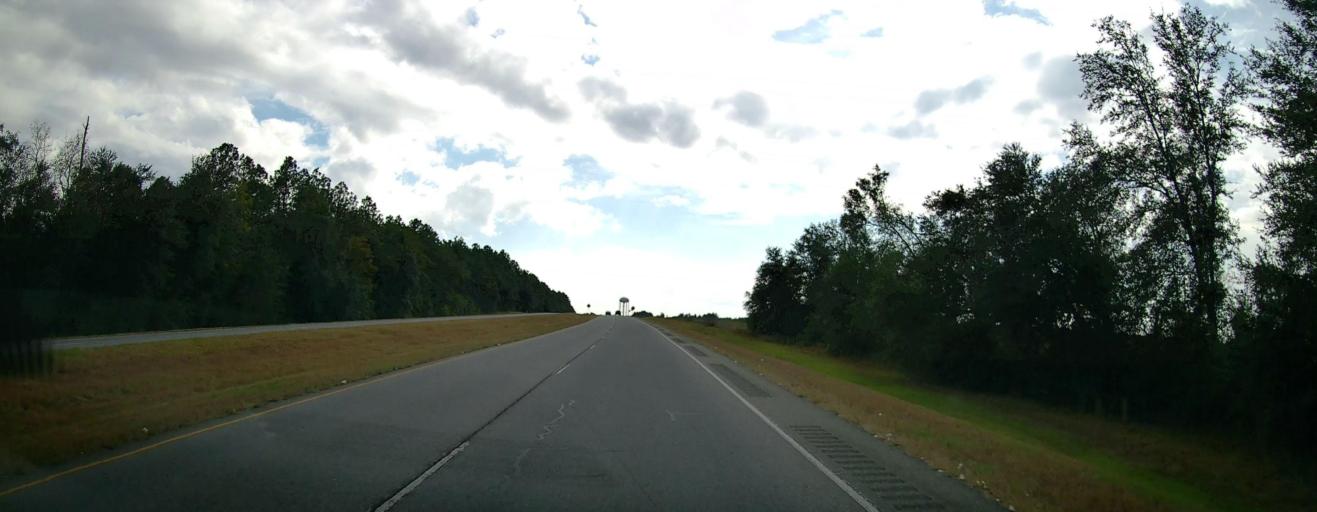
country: US
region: Georgia
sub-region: Mitchell County
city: Camilla
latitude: 31.2909
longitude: -84.1851
